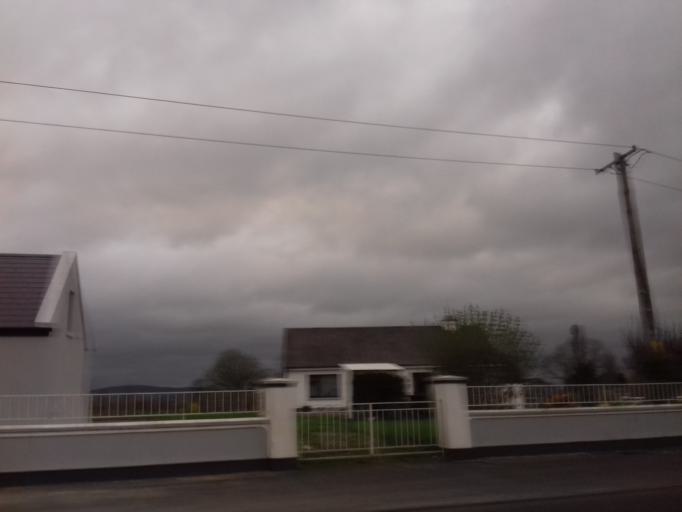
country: IE
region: Munster
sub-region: County Limerick
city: Newcastle West
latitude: 52.4738
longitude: -9.0183
